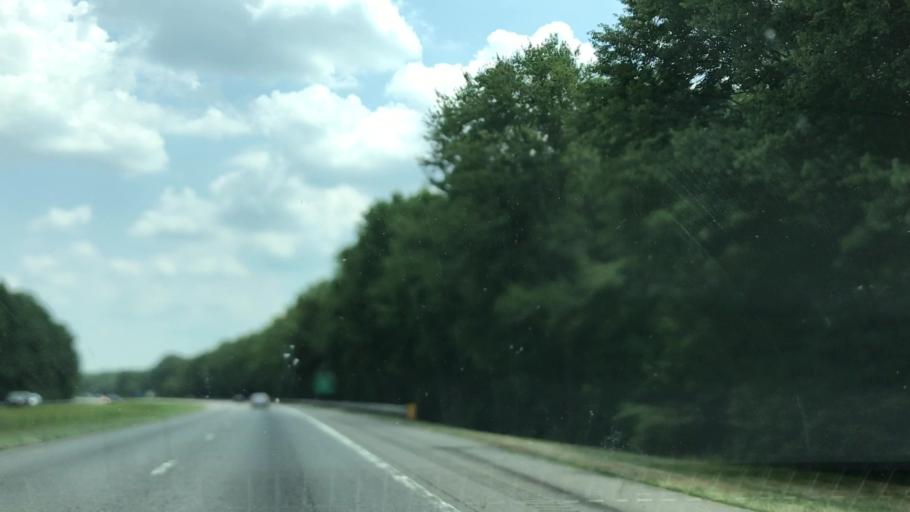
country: US
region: North Carolina
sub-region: Iredell County
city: Statesville
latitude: 35.8631
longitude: -80.8646
